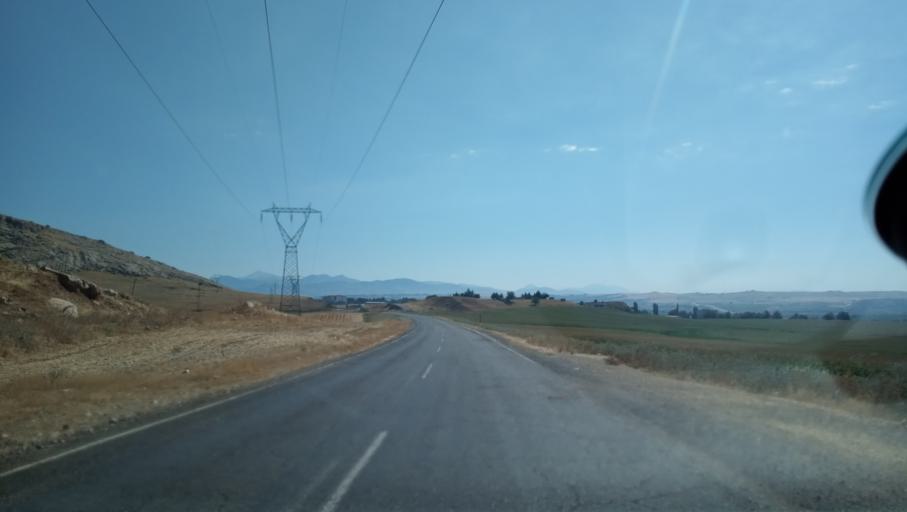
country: TR
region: Diyarbakir
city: Malabadi
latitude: 38.1301
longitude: 41.1810
